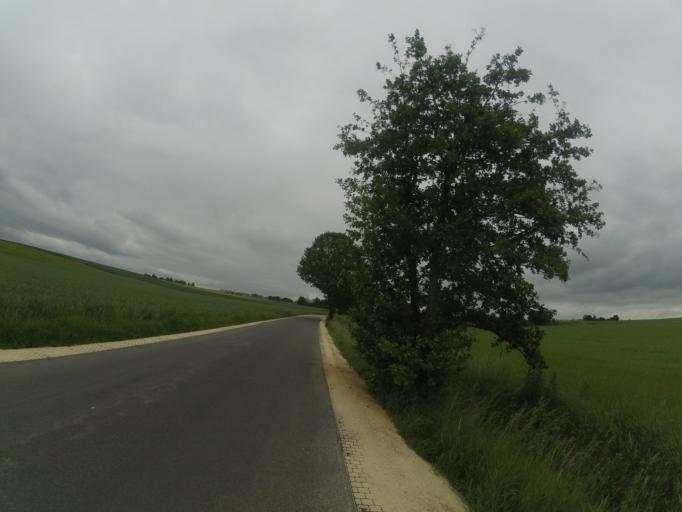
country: DE
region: Baden-Wuerttemberg
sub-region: Tuebingen Region
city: Langenau
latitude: 48.4996
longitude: 10.0897
